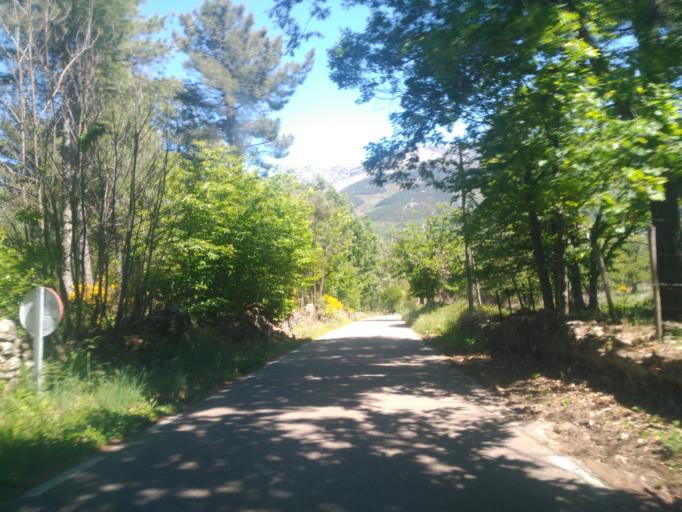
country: ES
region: Castille and Leon
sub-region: Provincia de Salamanca
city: Bejar
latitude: 40.3784
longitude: -5.7541
